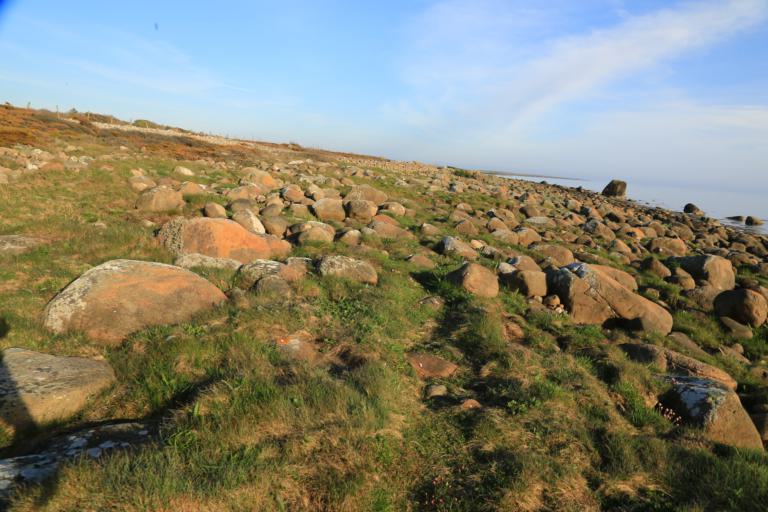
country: SE
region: Halland
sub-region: Varbergs Kommun
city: Traslovslage
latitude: 57.0386
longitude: 12.2931
